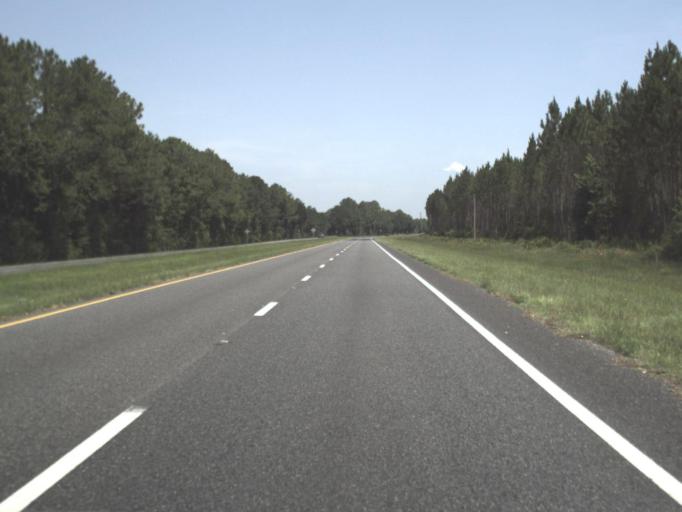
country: US
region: Florida
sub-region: Taylor County
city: Steinhatchee
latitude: 29.7292
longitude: -83.3124
